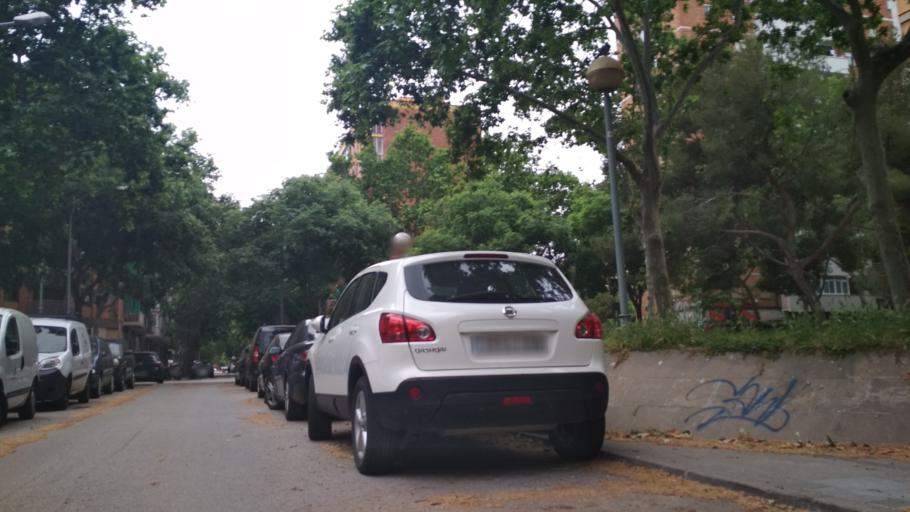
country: ES
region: Catalonia
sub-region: Provincia de Barcelona
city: Sant Marti
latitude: 41.4140
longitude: 2.1985
